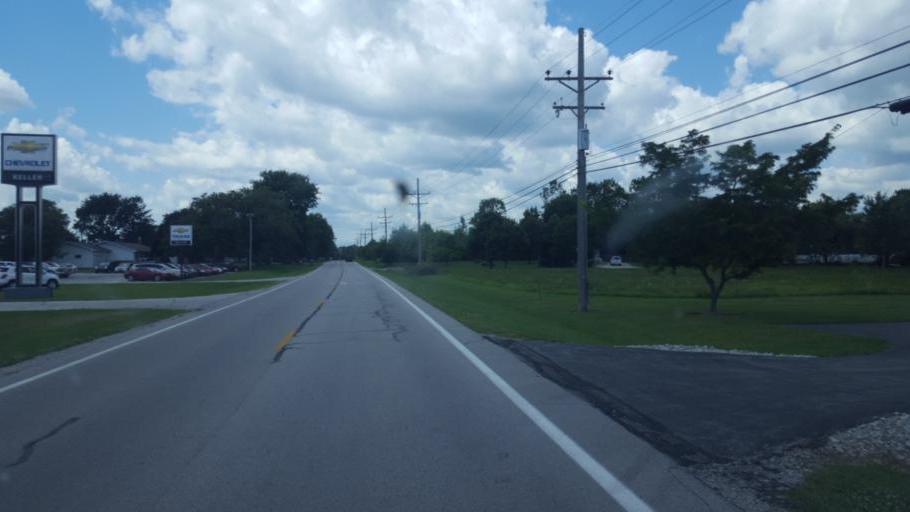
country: US
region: Ohio
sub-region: Sandusky County
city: Gibsonburg
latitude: 41.3848
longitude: -83.3015
